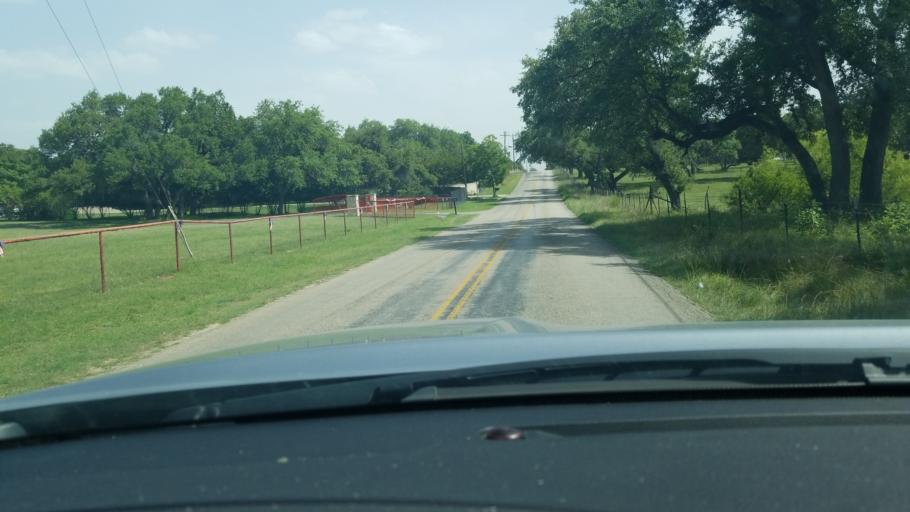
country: US
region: Texas
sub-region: Comal County
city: Bulverde
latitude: 29.7740
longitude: -98.4588
